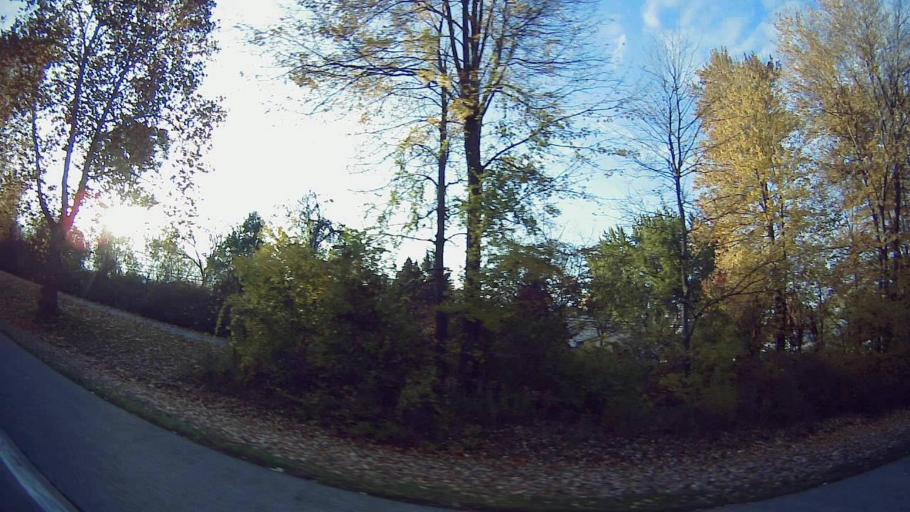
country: US
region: Michigan
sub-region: Macomb County
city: Fraser
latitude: 42.5679
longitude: -82.9539
